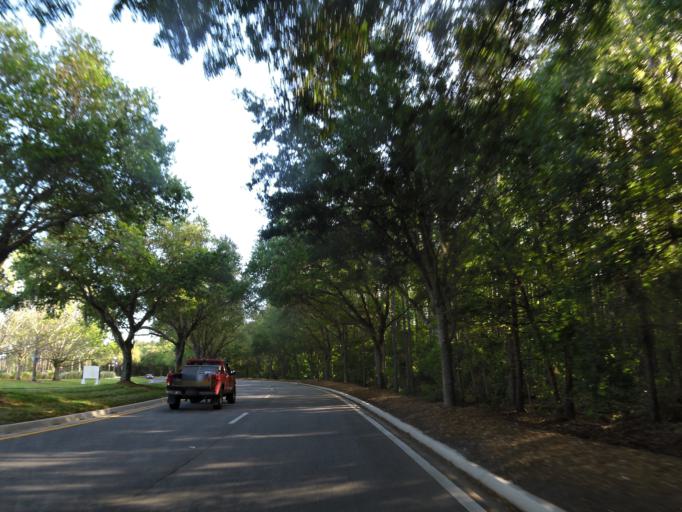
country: US
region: Florida
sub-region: Saint Johns County
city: Villano Beach
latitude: 29.9930
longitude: -81.4766
